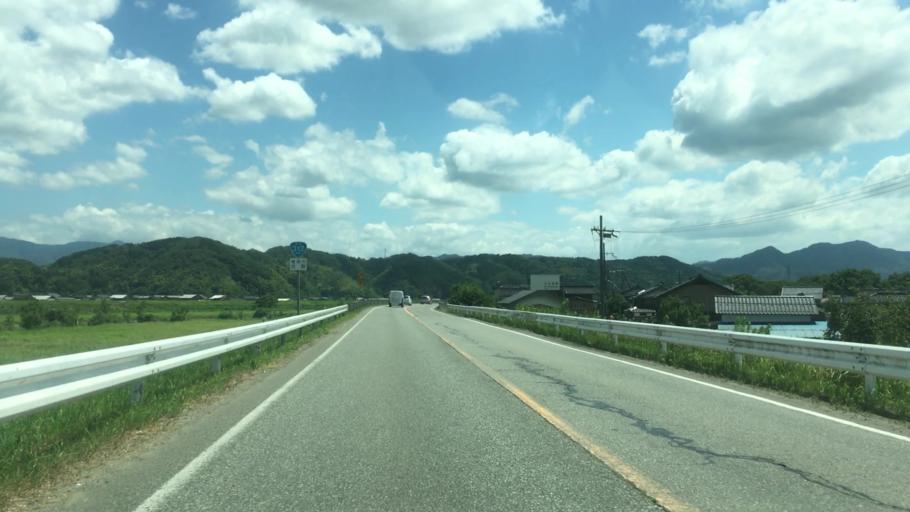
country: JP
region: Hyogo
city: Toyooka
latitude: 35.5141
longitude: 134.8213
